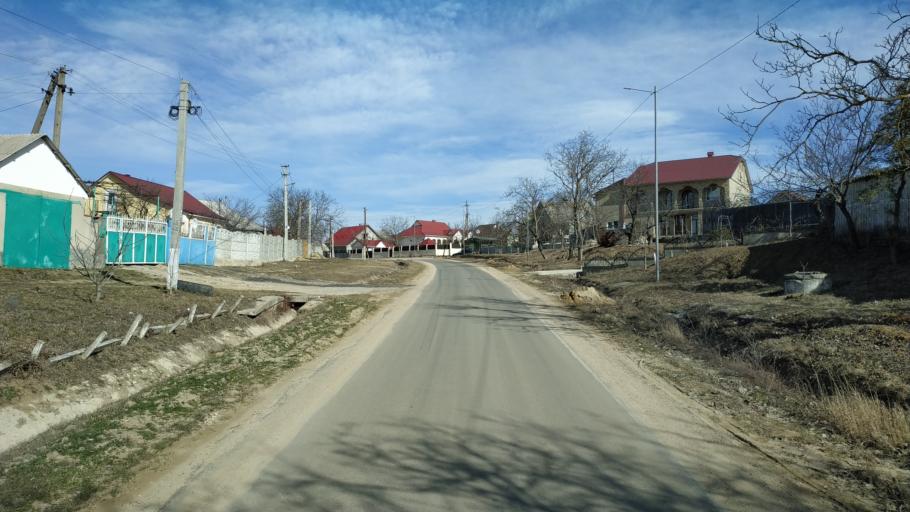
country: MD
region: Nisporeni
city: Nisporeni
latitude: 47.1015
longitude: 28.2957
